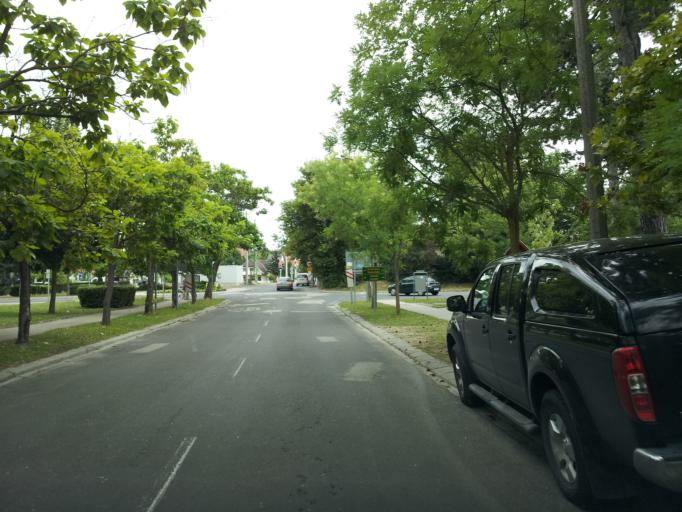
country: HU
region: Somogy
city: Siofok
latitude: 46.8987
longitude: 18.0176
